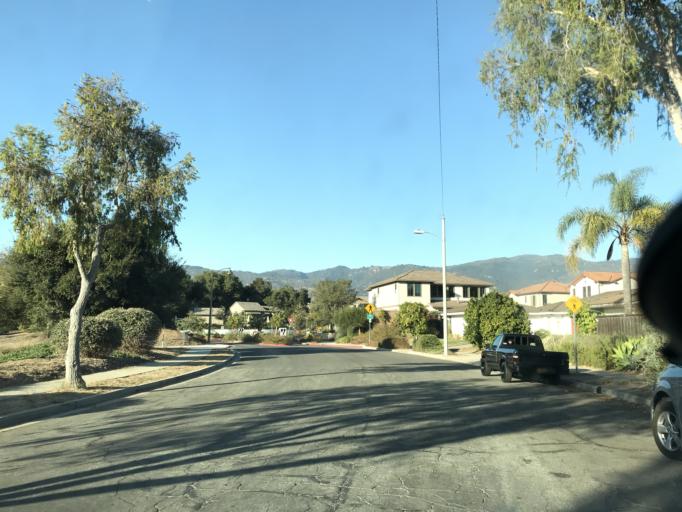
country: US
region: California
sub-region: Santa Barbara County
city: Goleta
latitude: 34.4481
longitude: -119.8144
